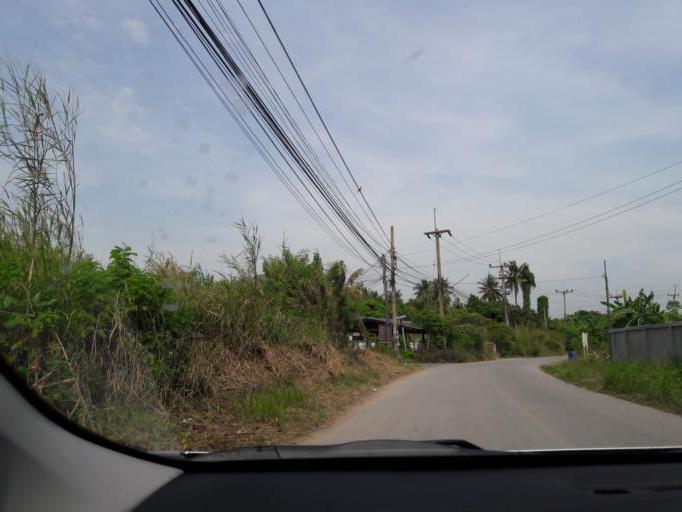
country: TH
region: Ang Thong
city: Ang Thong
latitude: 14.5844
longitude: 100.4624
